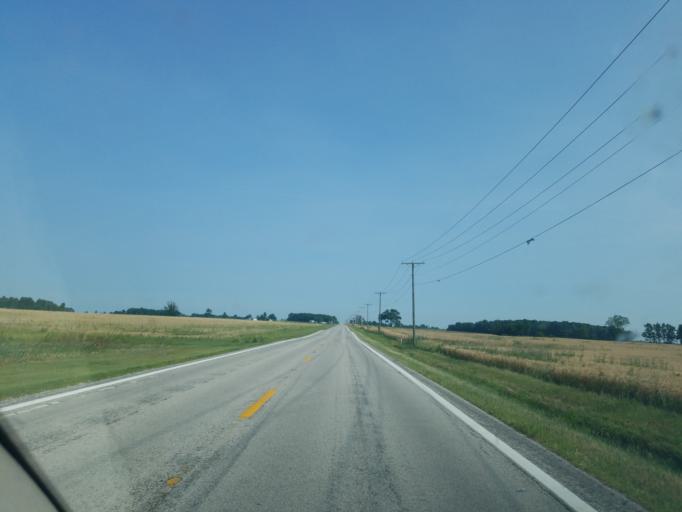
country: US
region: Ohio
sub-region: Wyandot County
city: Carey
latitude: 41.0243
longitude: -83.2942
